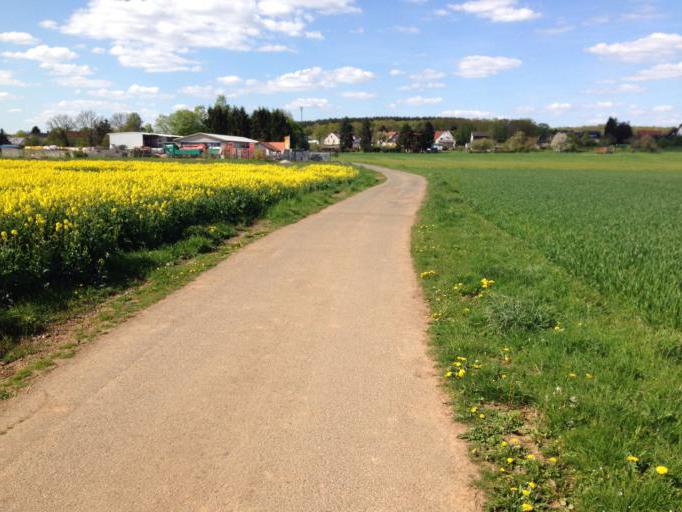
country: DE
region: Hesse
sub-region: Regierungsbezirk Giessen
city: Grunberg
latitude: 50.5481
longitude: 8.9235
